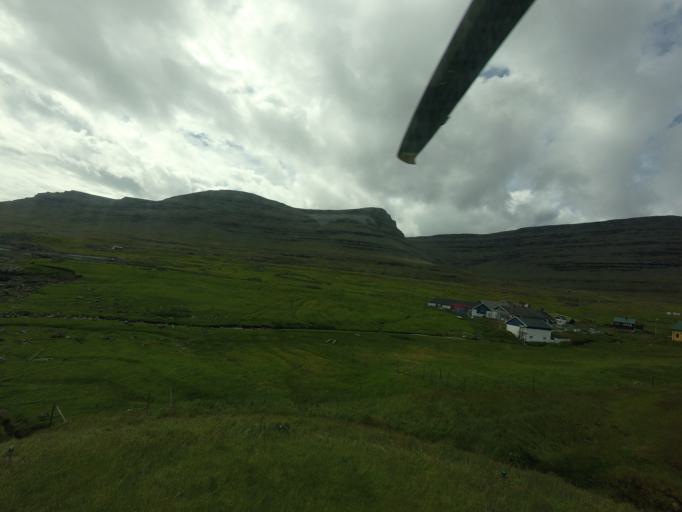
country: FO
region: Nordoyar
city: Klaksvik
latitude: 62.2770
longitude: -6.3404
